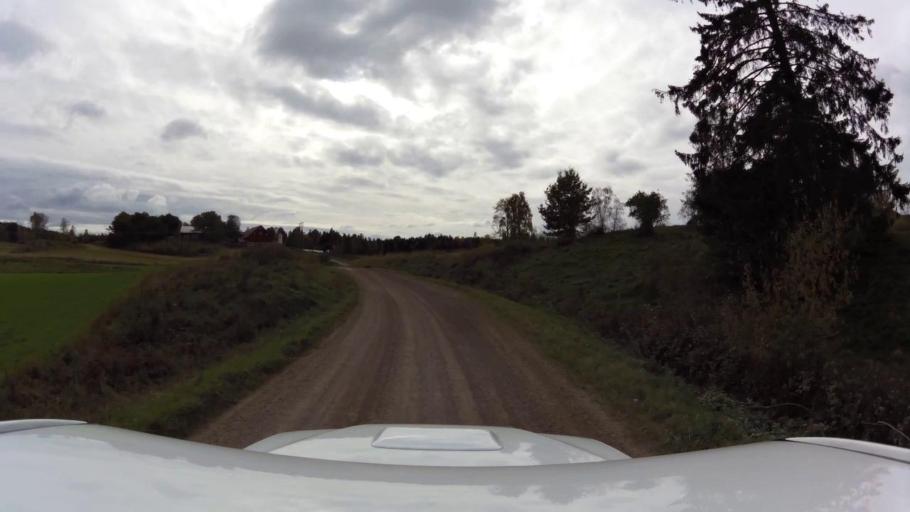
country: SE
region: OEstergoetland
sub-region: Linkopings Kommun
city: Ekangen
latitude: 58.5611
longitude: 15.6612
